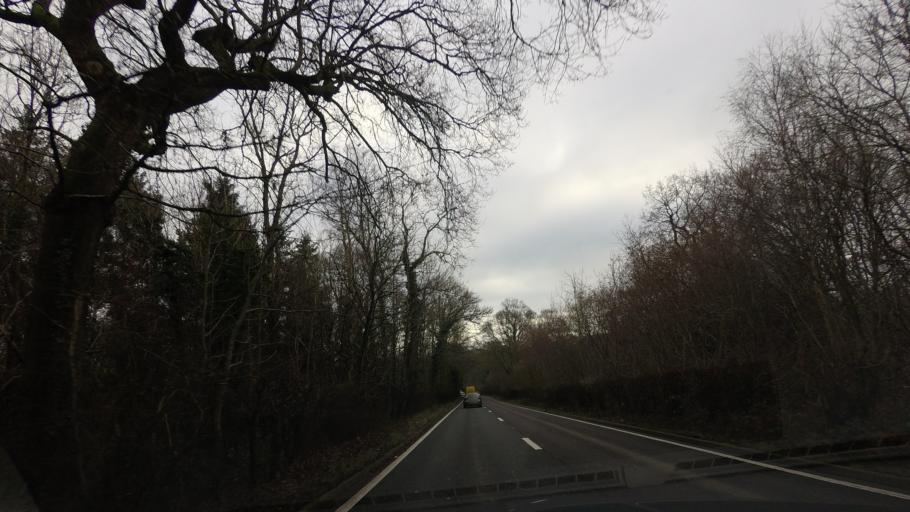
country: GB
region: England
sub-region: East Sussex
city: Wadhurst
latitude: 51.0895
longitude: 0.3979
